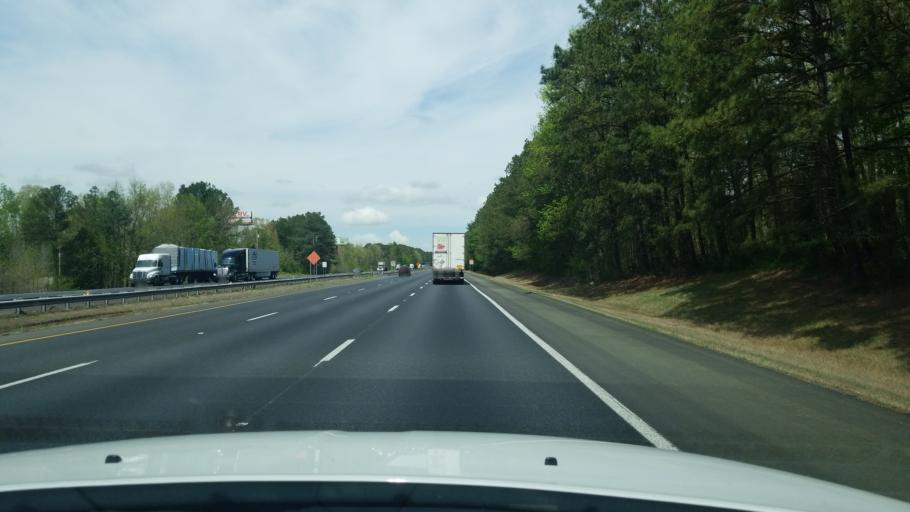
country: US
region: Georgia
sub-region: Gordon County
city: Calhoun
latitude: 34.6248
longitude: -84.9699
